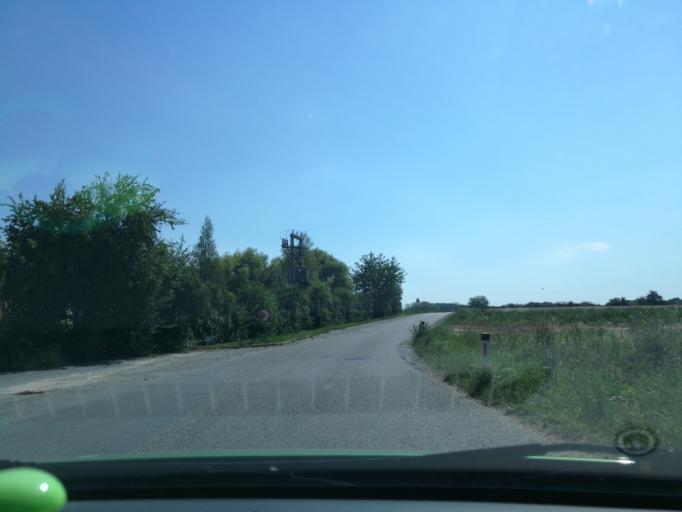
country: AT
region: Lower Austria
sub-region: Politischer Bezirk Ganserndorf
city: Ganserndorf
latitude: 48.3460
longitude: 16.7346
